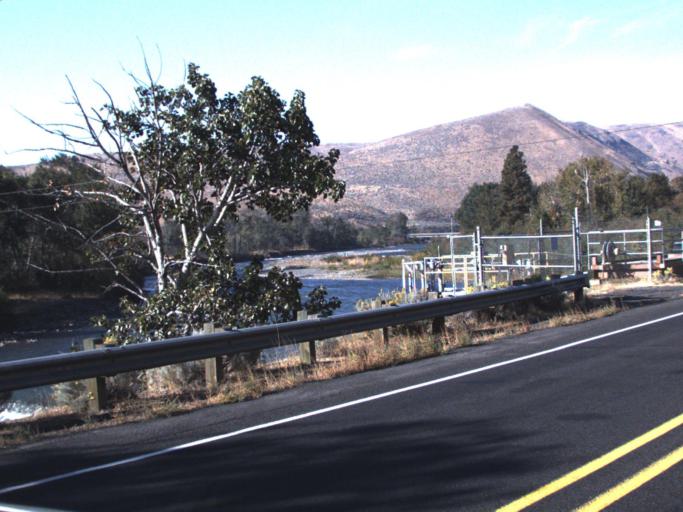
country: US
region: Washington
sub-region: Yakima County
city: Tieton
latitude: 46.7486
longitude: -120.7797
